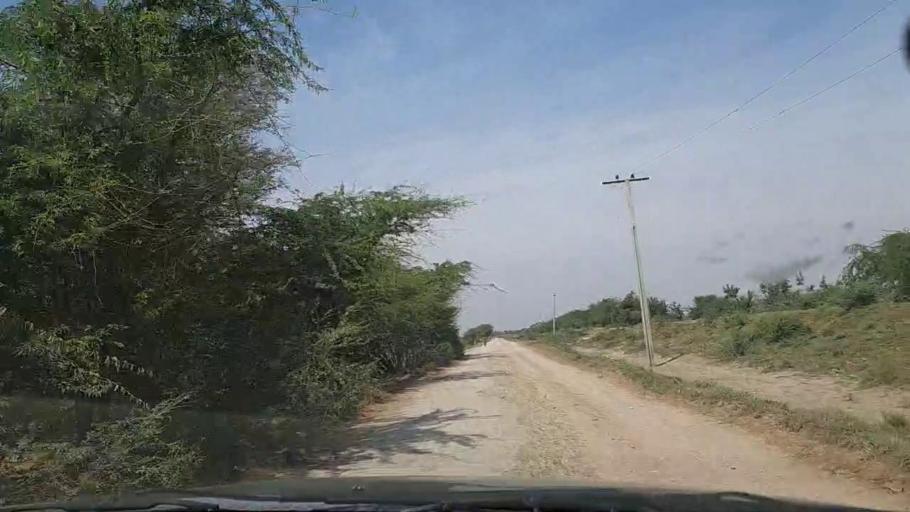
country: PK
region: Sindh
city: Mirpur Batoro
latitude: 24.6466
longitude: 68.1894
